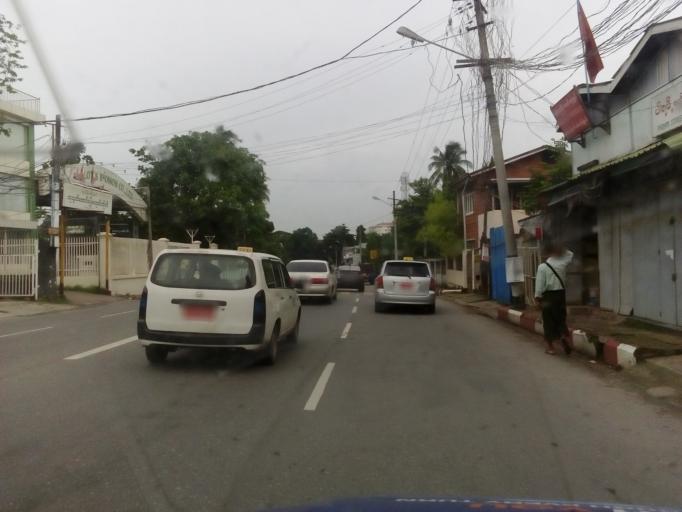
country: MM
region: Yangon
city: Yangon
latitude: 16.8519
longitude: 96.1503
